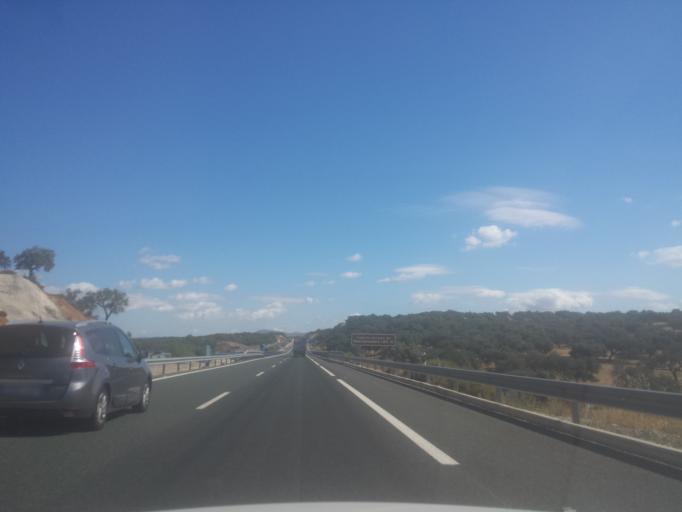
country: ES
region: Andalusia
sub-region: Provincia de Huelva
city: Santa Olalla del Cala
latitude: 37.8831
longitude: -6.2195
